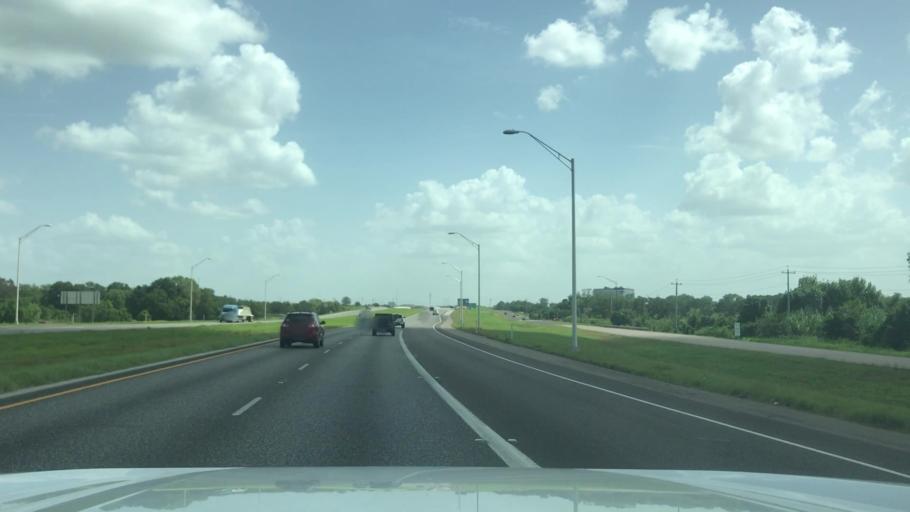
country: US
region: Texas
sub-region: Brazos County
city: College Station
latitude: 30.6079
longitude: -96.2903
